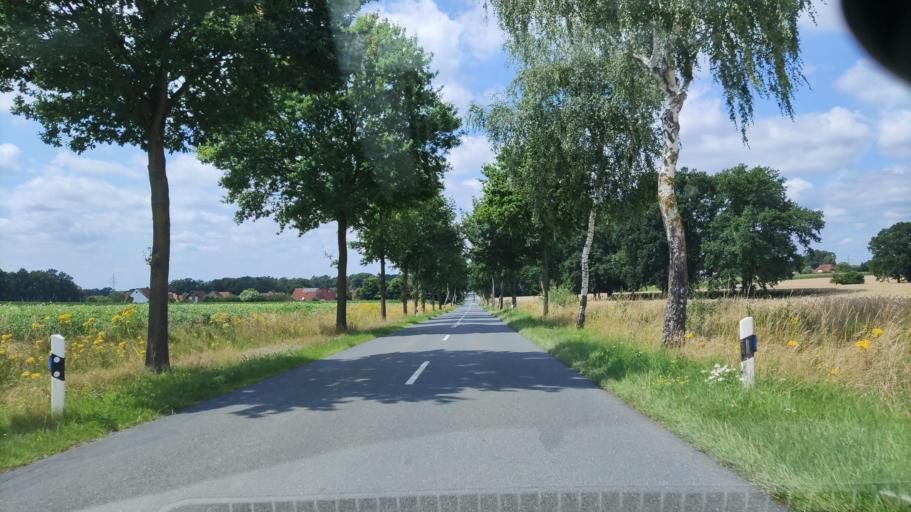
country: DE
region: Lower Saxony
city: Bad Fallingbostel
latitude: 52.8288
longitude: 9.6527
